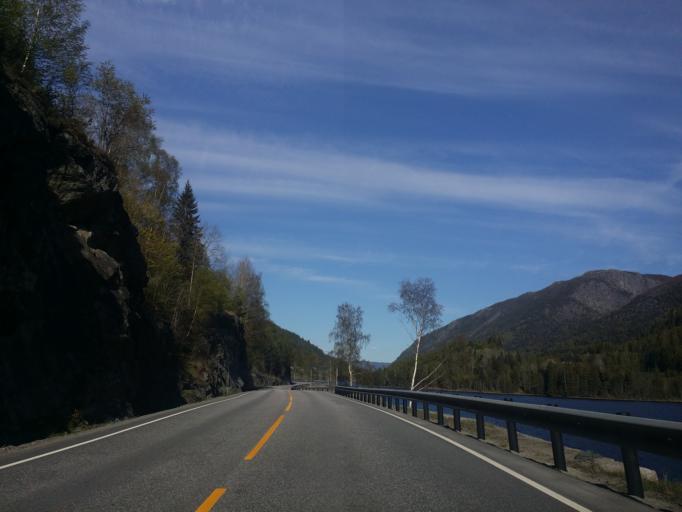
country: NO
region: Telemark
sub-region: Seljord
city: Seljord
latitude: 59.6058
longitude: 8.7374
